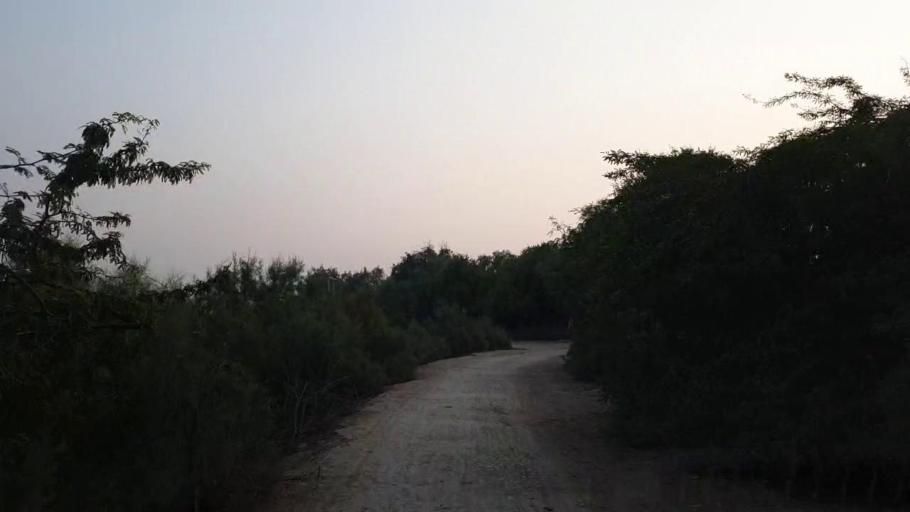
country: PK
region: Sindh
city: Bhan
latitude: 26.5323
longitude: 67.7062
